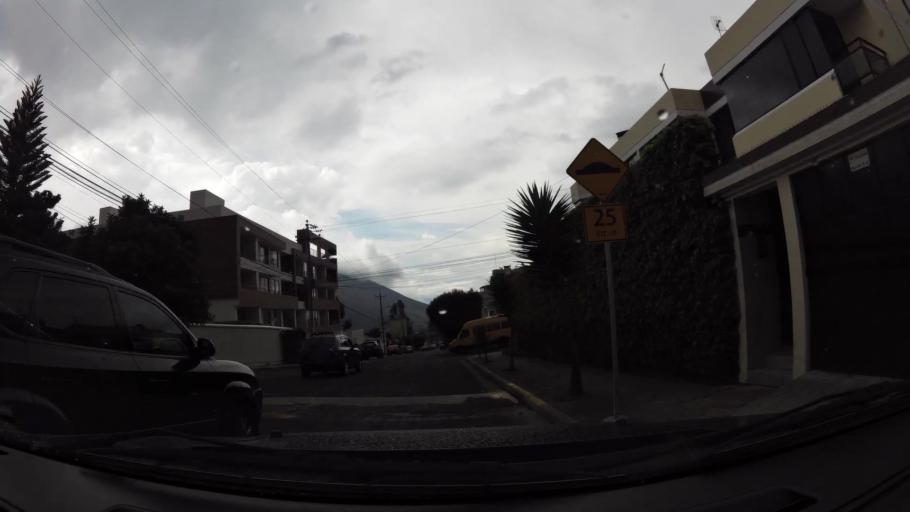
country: EC
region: Pichincha
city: Quito
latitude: -0.0968
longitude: -78.4805
